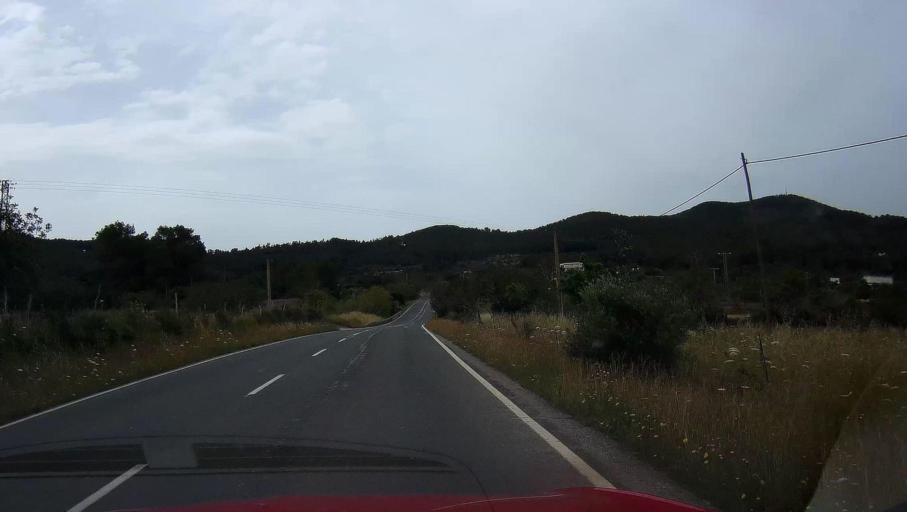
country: ES
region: Balearic Islands
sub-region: Illes Balears
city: Sant Joan de Labritja
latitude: 39.0902
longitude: 1.5026
